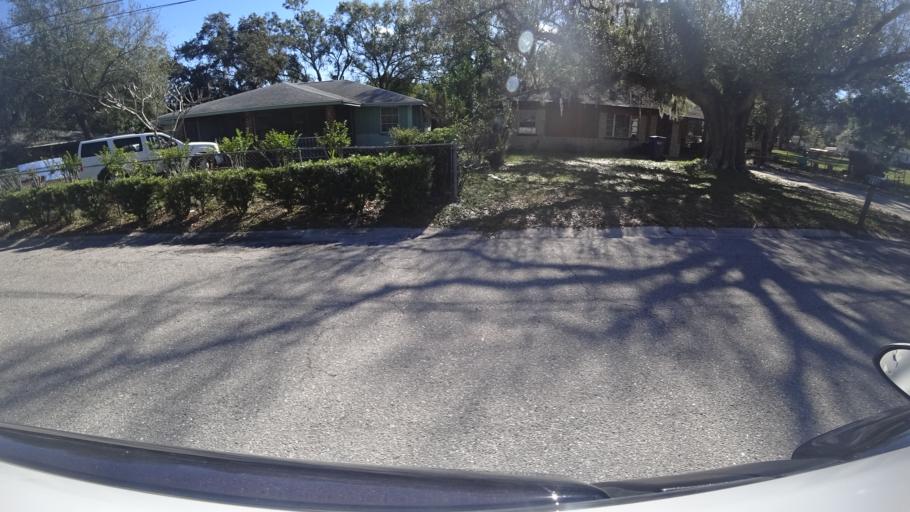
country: US
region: Florida
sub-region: Manatee County
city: Whitfield
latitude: 27.4353
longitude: -82.5540
